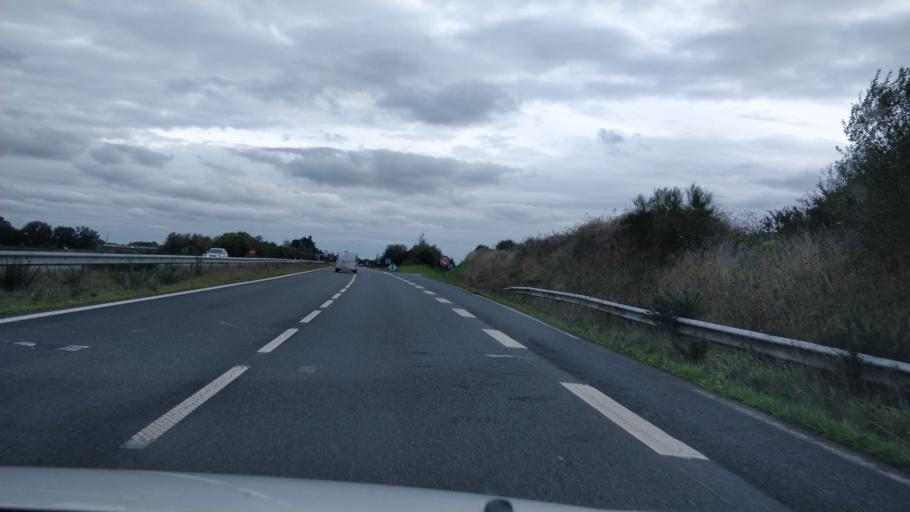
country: FR
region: Brittany
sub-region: Departement des Cotes-d'Armor
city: Plehedel
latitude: 48.6587
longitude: -3.0210
